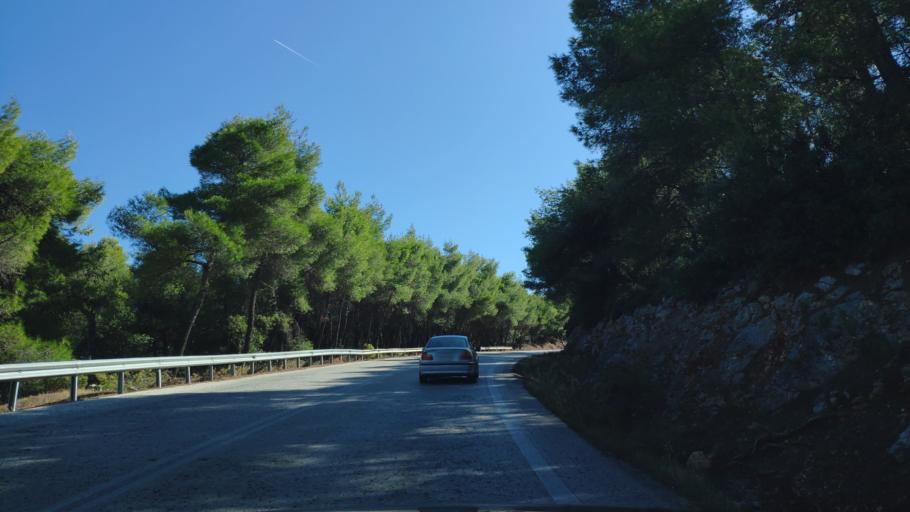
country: GR
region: Peloponnese
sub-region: Nomos Korinthias
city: Sofikon
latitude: 37.8259
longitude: 23.1016
